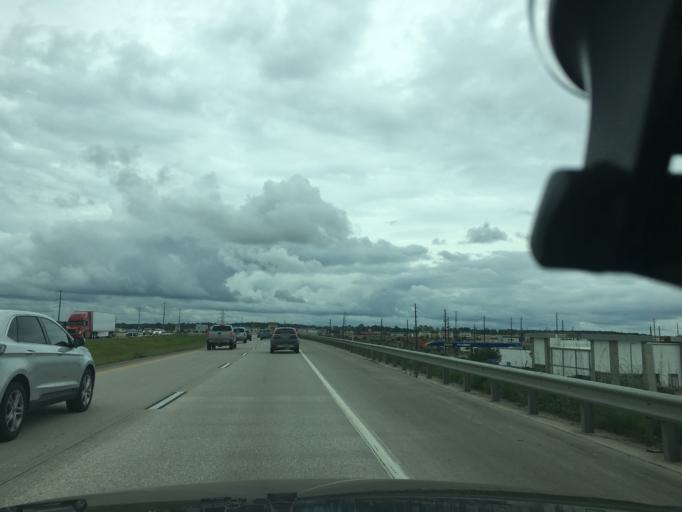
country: US
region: Texas
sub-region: Montgomery County
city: The Woodlands
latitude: 30.0866
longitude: -95.5289
